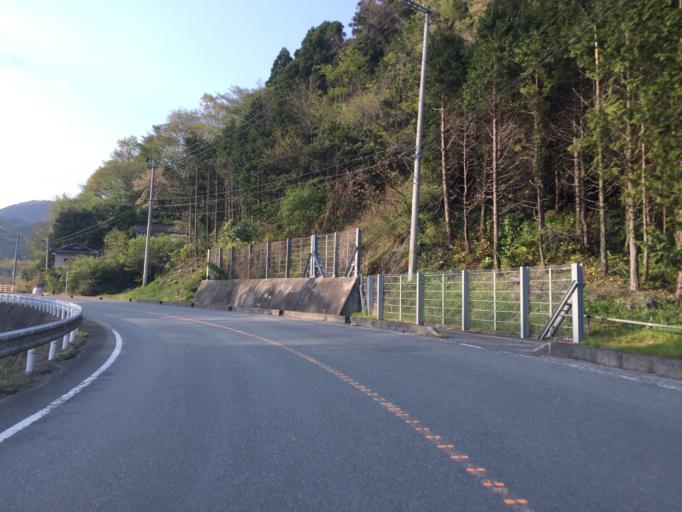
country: JP
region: Fukushima
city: Iwaki
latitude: 37.0737
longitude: 140.8064
